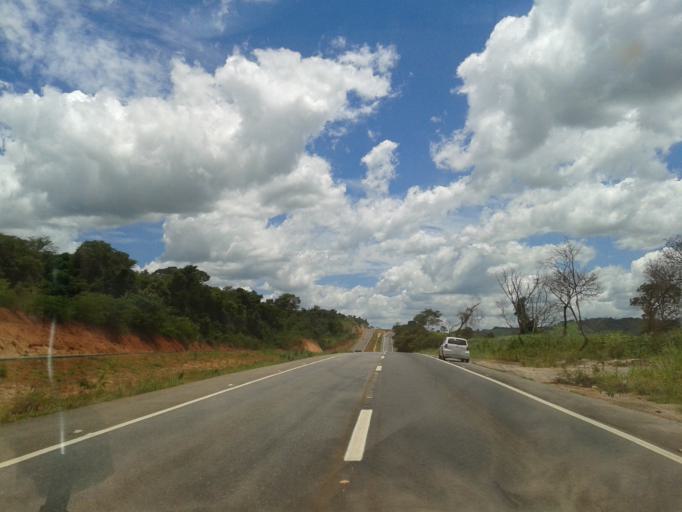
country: BR
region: Goias
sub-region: Petrolina De Goias
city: Petrolina de Goias
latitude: -16.1834
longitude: -49.3242
